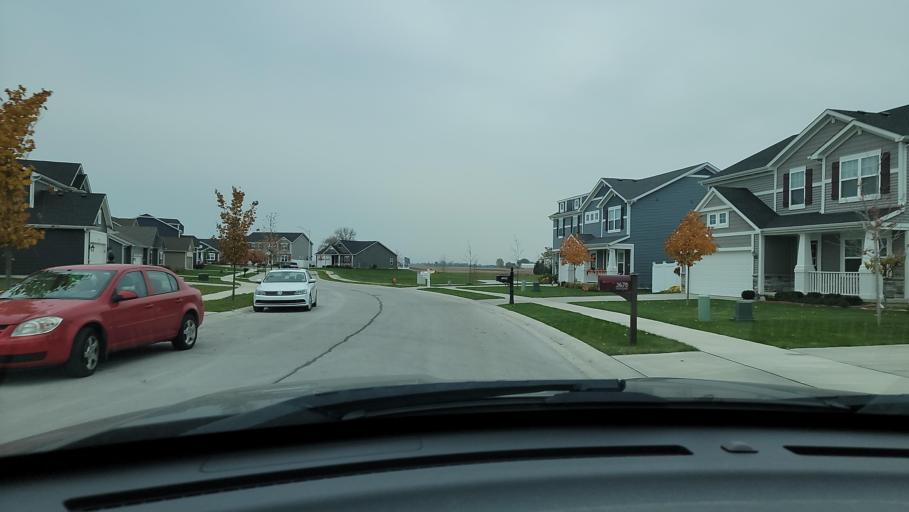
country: US
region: Indiana
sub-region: Porter County
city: Portage
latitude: 41.5452
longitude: -87.1707
